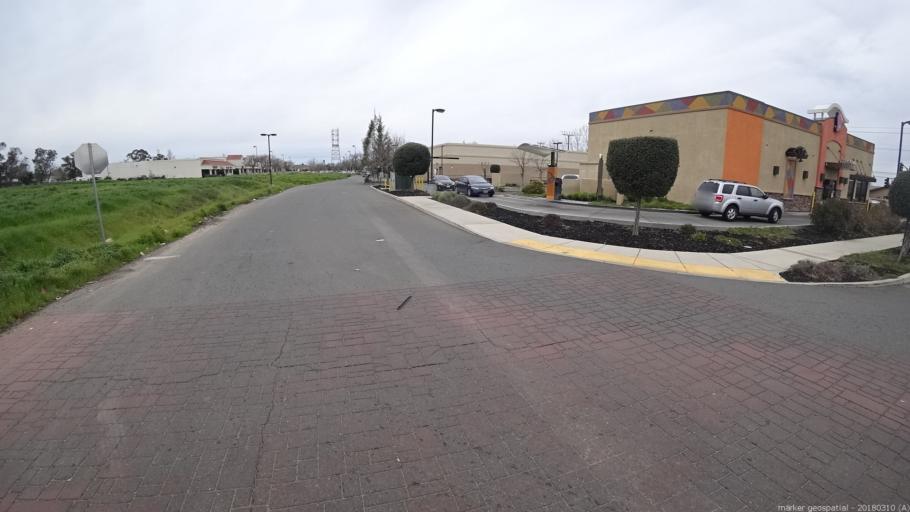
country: US
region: California
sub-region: Sacramento County
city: Florin
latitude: 38.4811
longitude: -121.4053
